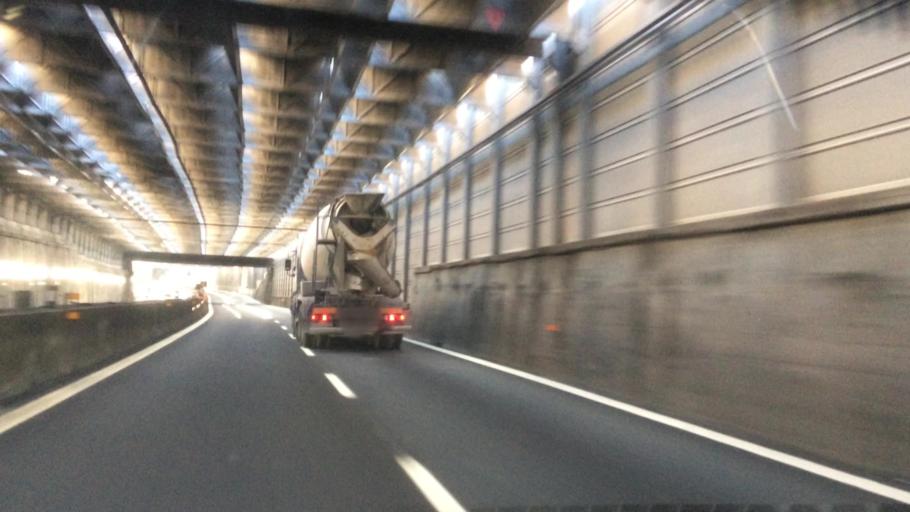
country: IT
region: Liguria
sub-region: Provincia di Genova
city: San Teodoro
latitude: 44.4306
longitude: 8.8436
